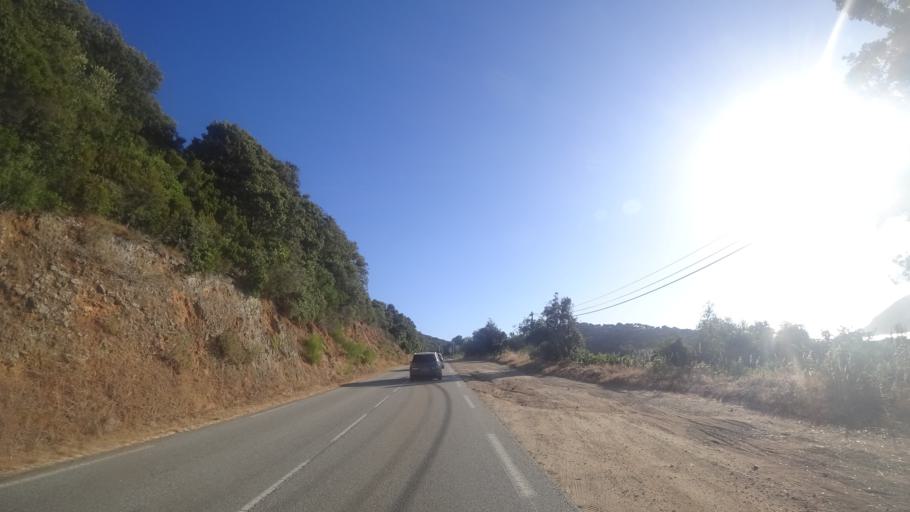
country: FR
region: Corsica
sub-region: Departement de la Corse-du-Sud
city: Cargese
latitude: 42.1668
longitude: 8.6038
